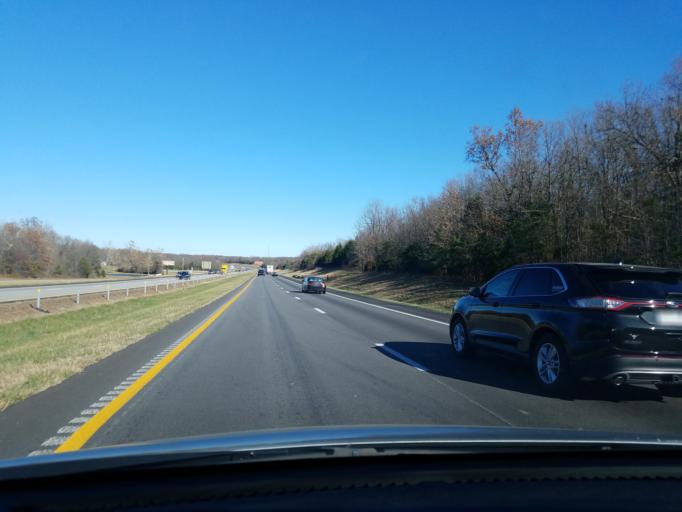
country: US
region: Missouri
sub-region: Webster County
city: Marshfield
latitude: 37.3518
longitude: -92.9193
